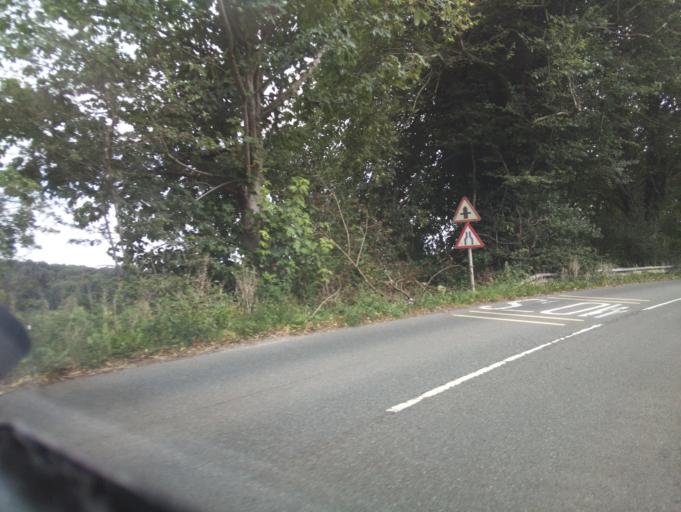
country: GB
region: England
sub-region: Devon
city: Totnes
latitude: 50.4329
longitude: -3.7162
